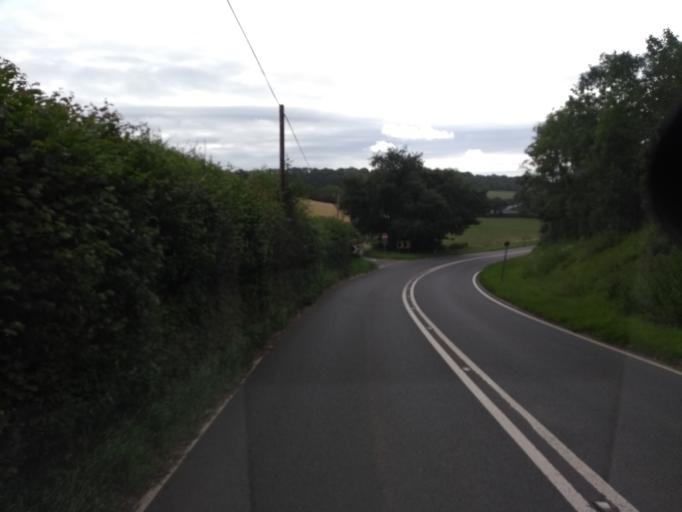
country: GB
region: England
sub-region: Somerset
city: Wiveliscombe
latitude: 51.0401
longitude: -3.2849
